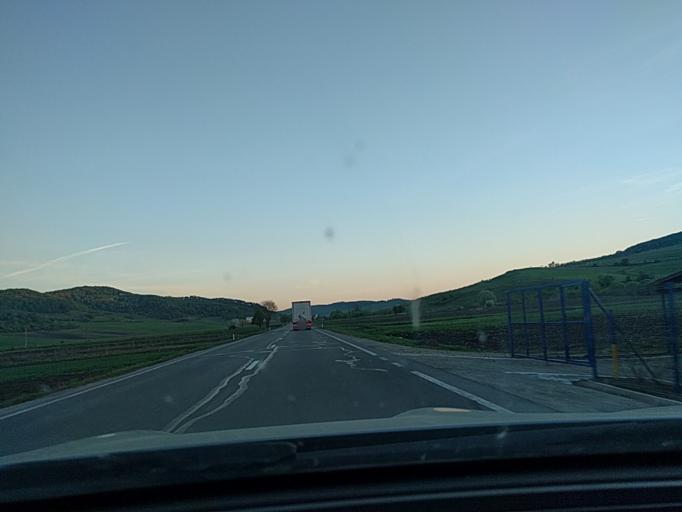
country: RO
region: Mures
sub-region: Comuna Balauseri
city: Chendu
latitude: 46.3734
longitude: 24.7261
